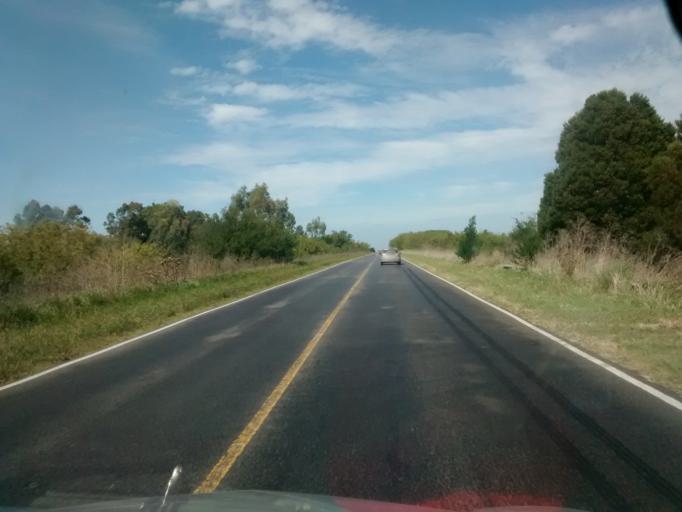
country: AR
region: Buenos Aires
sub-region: Partido de Ayacucho
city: Ayacucho
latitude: -36.7073
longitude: -58.5745
